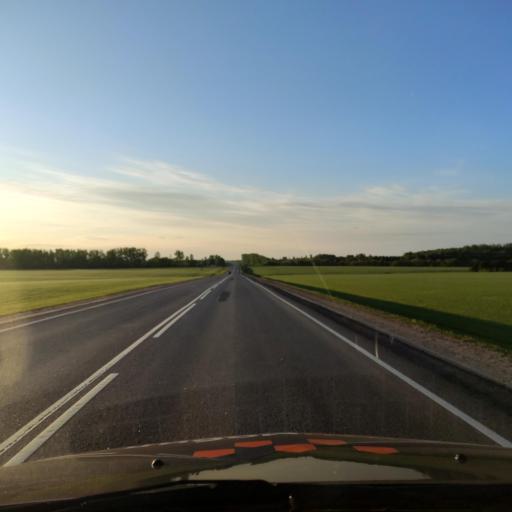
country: RU
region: Orjol
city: Livny
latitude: 52.4464
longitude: 37.5238
